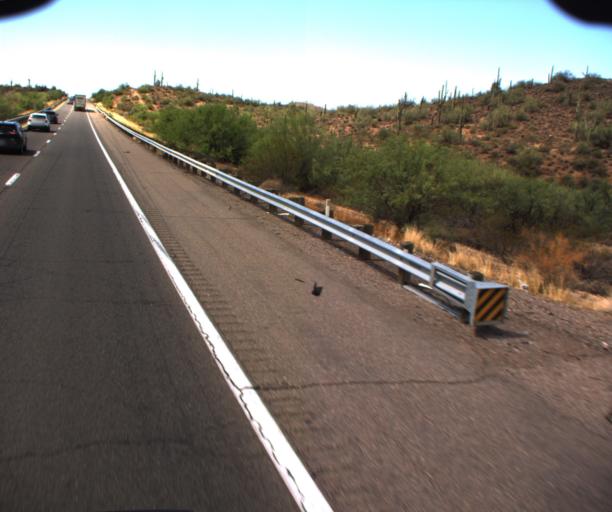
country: US
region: Arizona
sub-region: Maricopa County
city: New River
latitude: 33.9414
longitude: -112.1412
